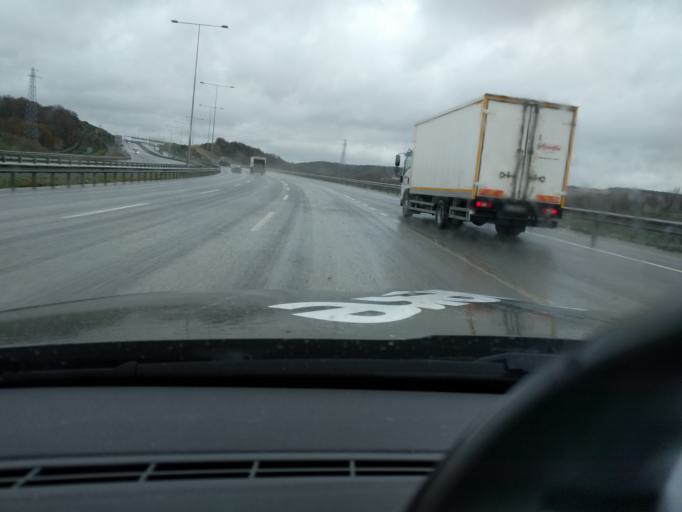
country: TR
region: Istanbul
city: Kemerburgaz
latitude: 41.2090
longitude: 28.8415
